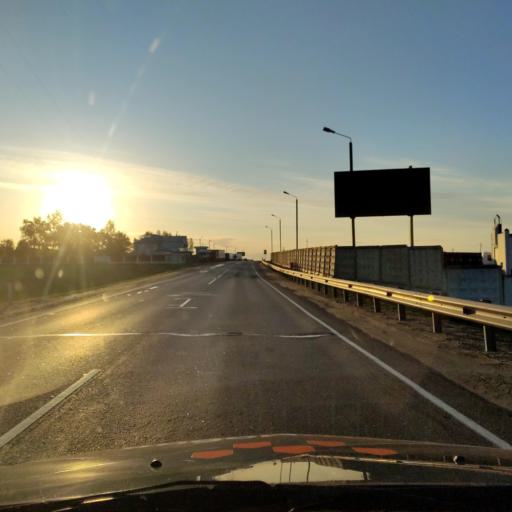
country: RU
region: Orjol
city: Livny
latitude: 52.4496
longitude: 37.4981
